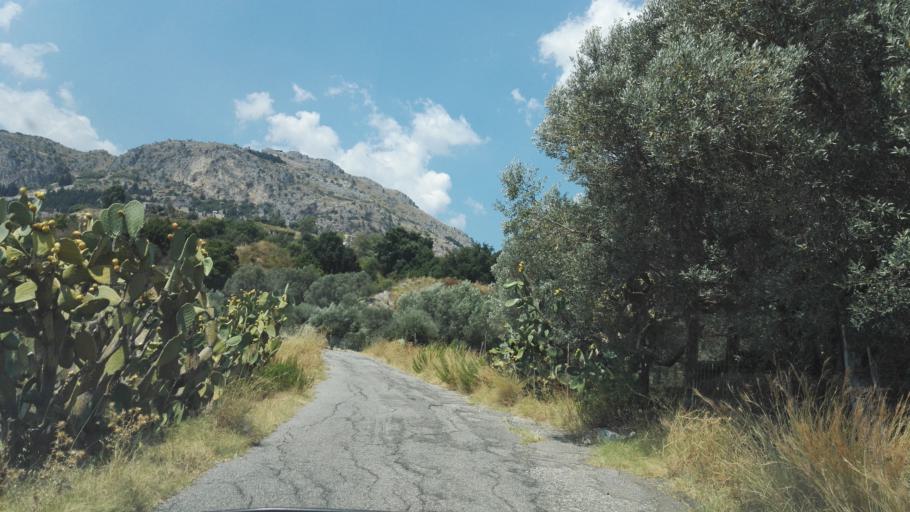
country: IT
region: Calabria
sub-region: Provincia di Reggio Calabria
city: Stilo
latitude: 38.4734
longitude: 16.4746
